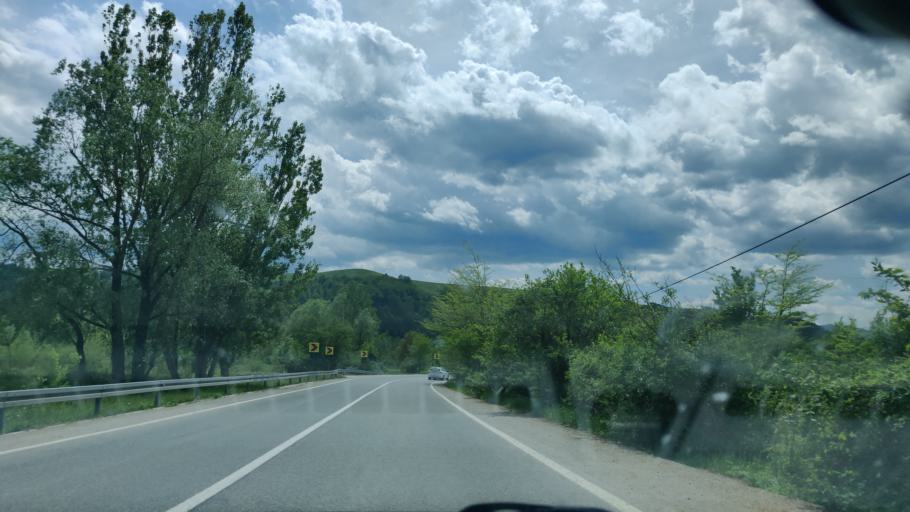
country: RO
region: Vrancea
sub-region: Comuna Negrilesti
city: Negrilesti
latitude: 45.9247
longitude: 26.7107
